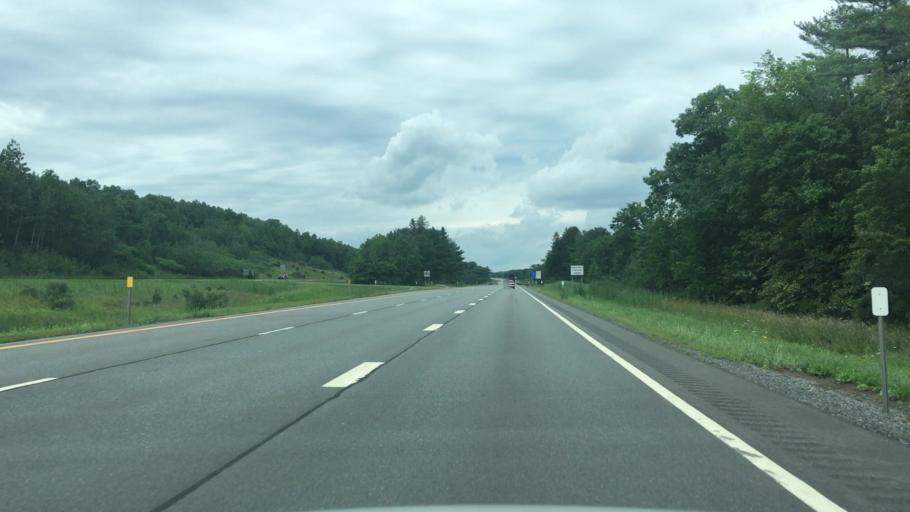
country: US
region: New York
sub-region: Albany County
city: Altamont
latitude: 42.7721
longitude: -74.0714
